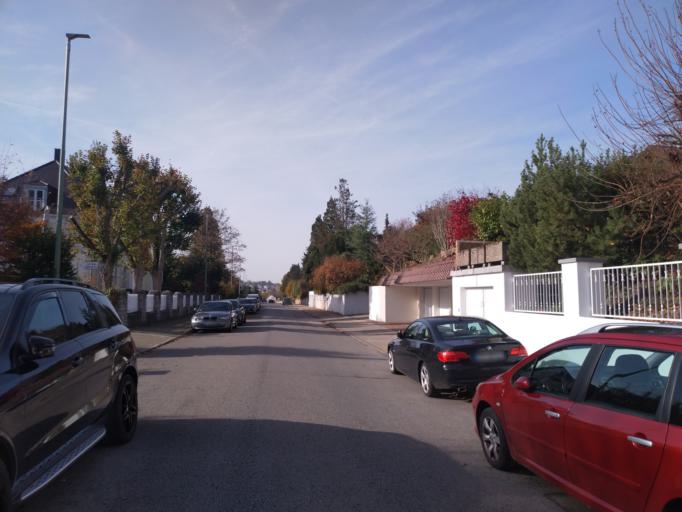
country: DE
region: Baden-Wuerttemberg
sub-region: Karlsruhe Region
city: Pforzheim
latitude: 48.8765
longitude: 8.6907
